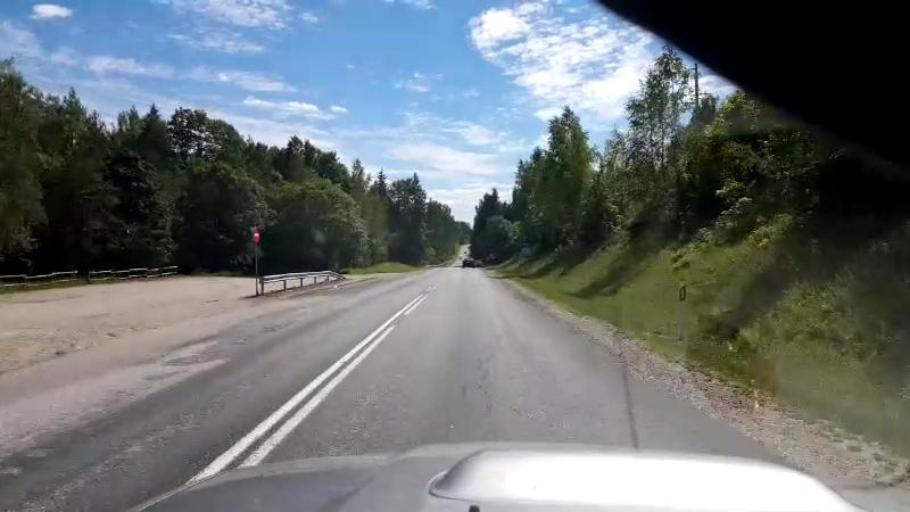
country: EE
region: Laeaene-Virumaa
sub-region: Rakke vald
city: Rakke
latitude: 58.8465
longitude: 26.2910
